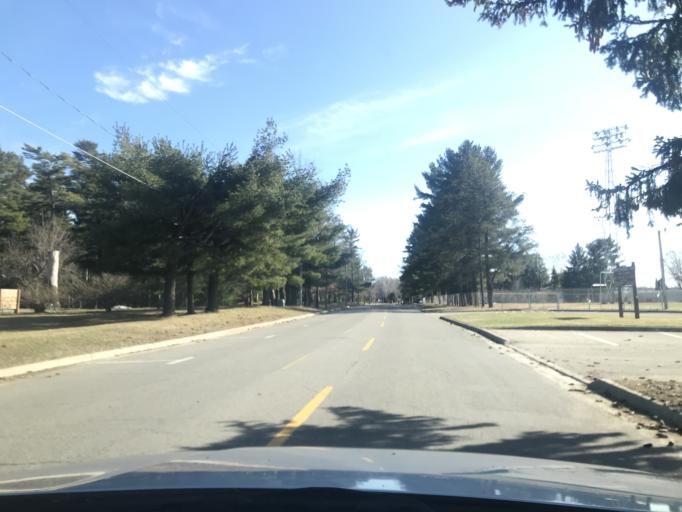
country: US
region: Wisconsin
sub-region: Marinette County
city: Marinette
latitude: 45.0917
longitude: -87.6398
